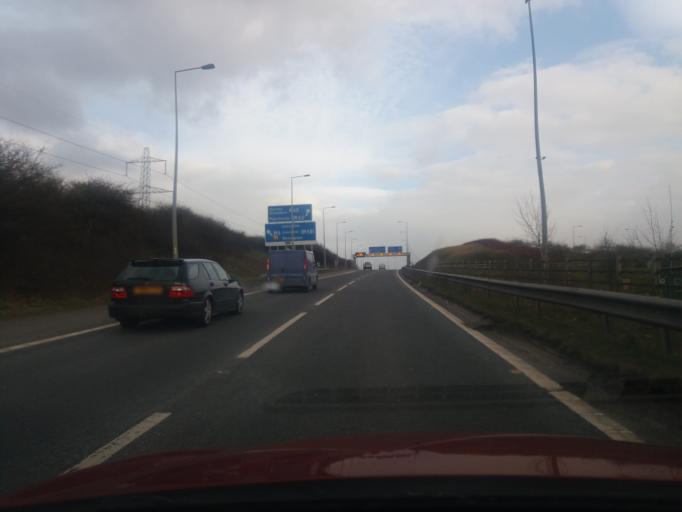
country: GB
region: England
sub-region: Lancashire
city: Clayton-le-Woods
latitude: 53.7181
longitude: -2.6721
